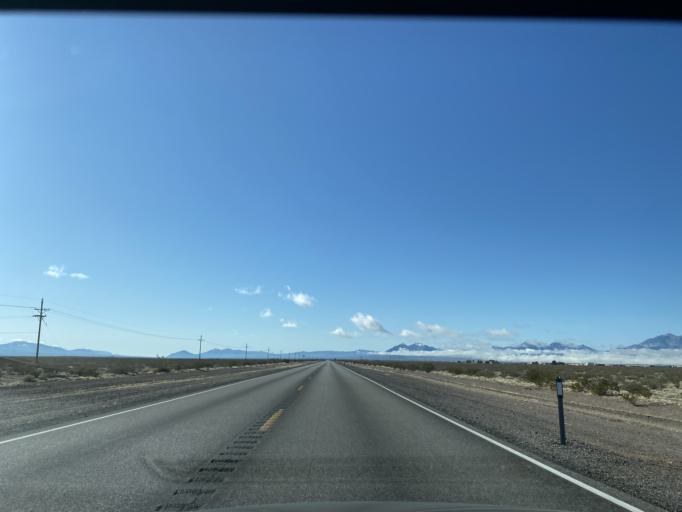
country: US
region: Nevada
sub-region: Nye County
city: Beatty
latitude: 36.5775
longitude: -116.4121
